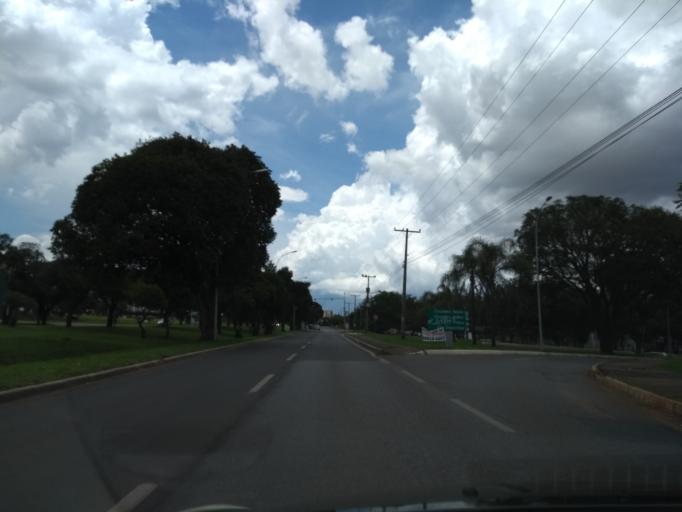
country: BR
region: Federal District
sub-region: Brasilia
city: Brasilia
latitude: -15.7894
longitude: -47.9326
